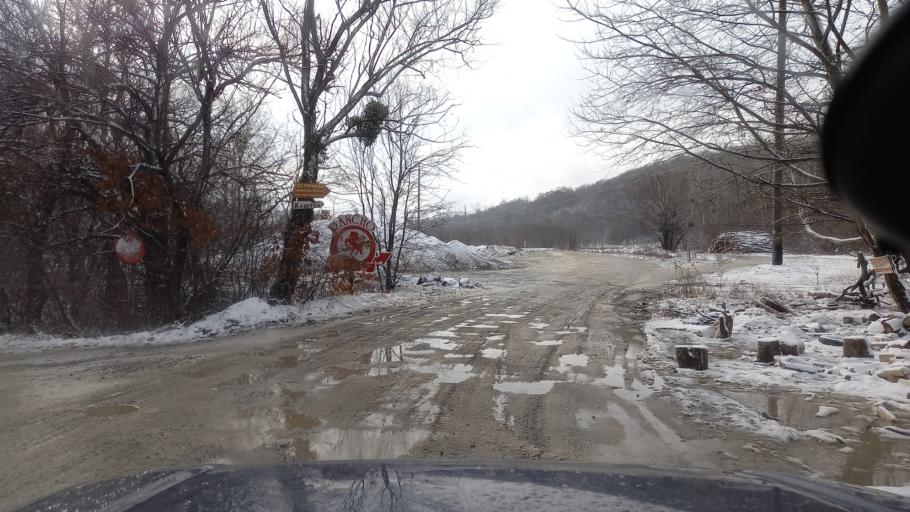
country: RU
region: Adygeya
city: Kamennomostskiy
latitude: 44.2467
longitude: 40.1986
